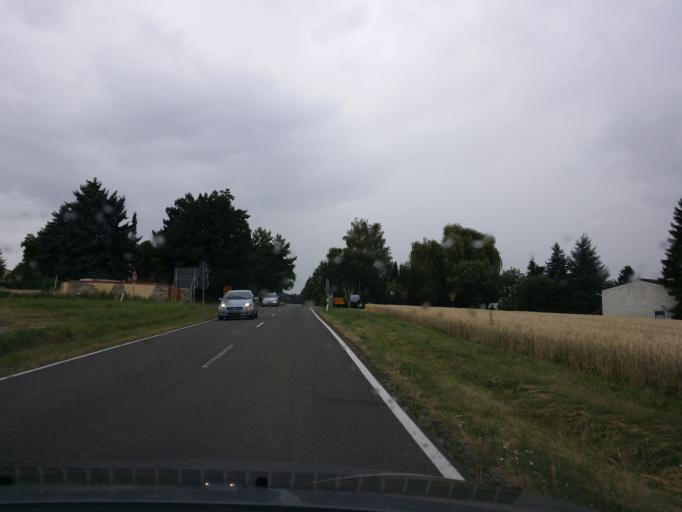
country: DE
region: Rheinland-Pfalz
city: Bechtolsheim
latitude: 49.8002
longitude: 8.1848
